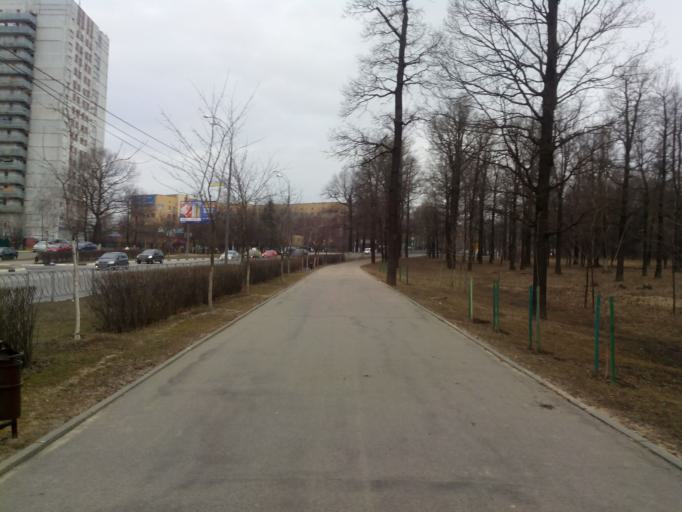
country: RU
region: Moskovskaya
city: Odintsovo
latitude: 55.6810
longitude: 37.2728
